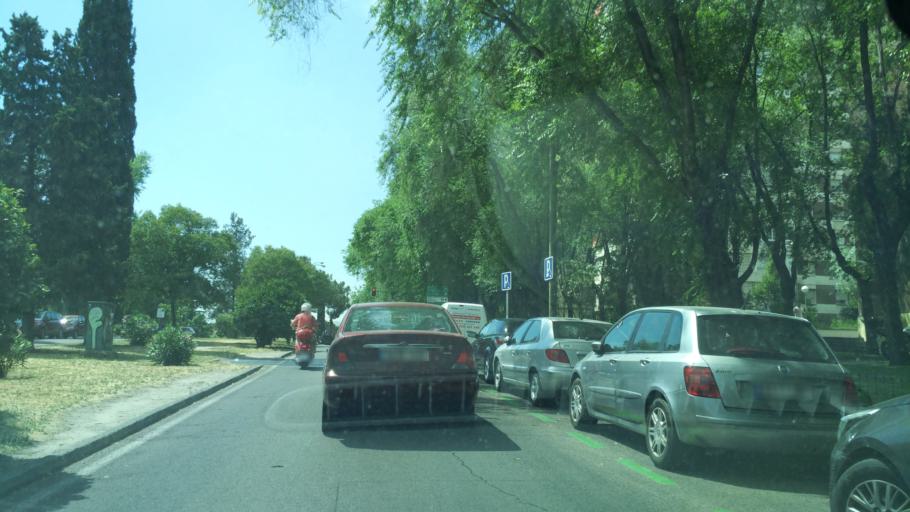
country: ES
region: Madrid
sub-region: Provincia de Madrid
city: Tetuan de las Victorias
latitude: 40.4757
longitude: -3.7030
